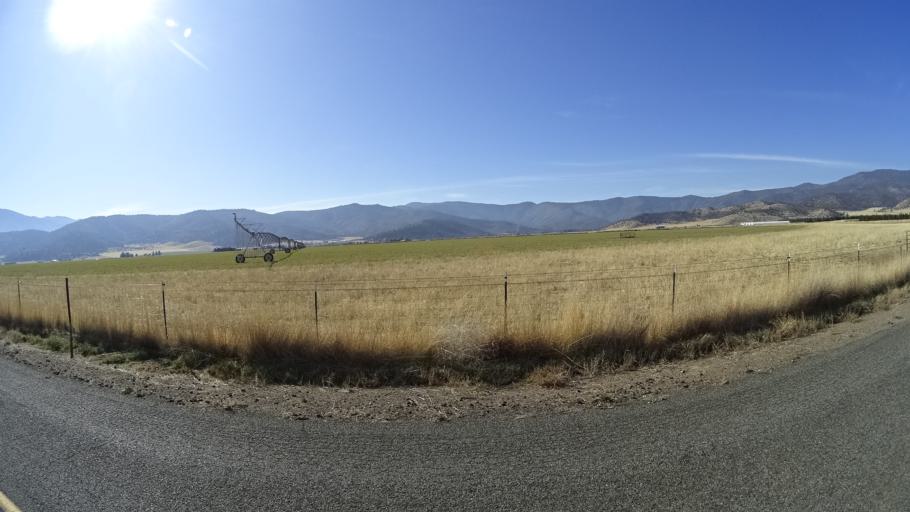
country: US
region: California
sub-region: Siskiyou County
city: Montague
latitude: 41.5492
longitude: -122.5433
